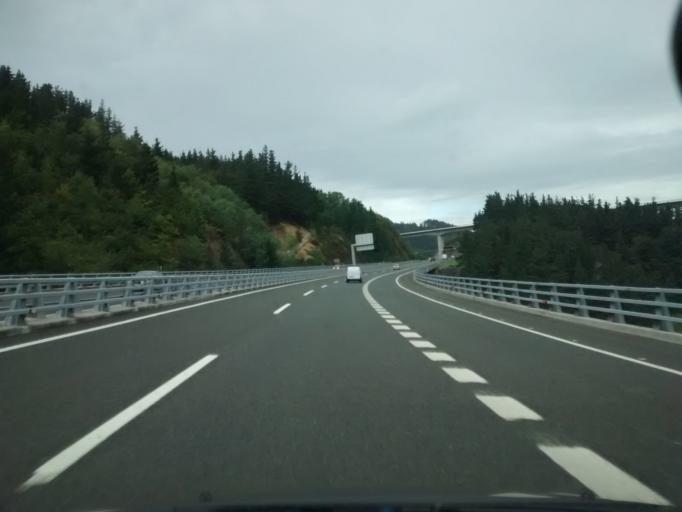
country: ES
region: Basque Country
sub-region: Provincia de Guipuzcoa
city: Bergara
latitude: 43.0933
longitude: -2.4350
